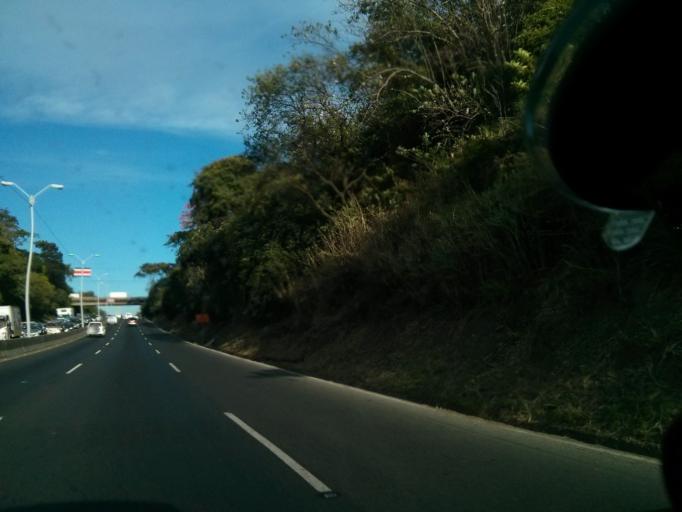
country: CR
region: Heredia
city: San Francisco
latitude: 9.9676
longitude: -84.1349
